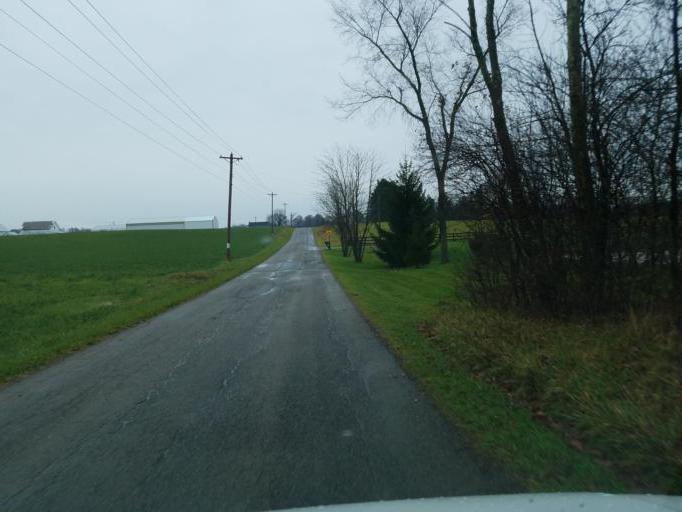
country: US
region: Ohio
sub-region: Knox County
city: Centerburg
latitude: 40.3489
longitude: -82.7294
